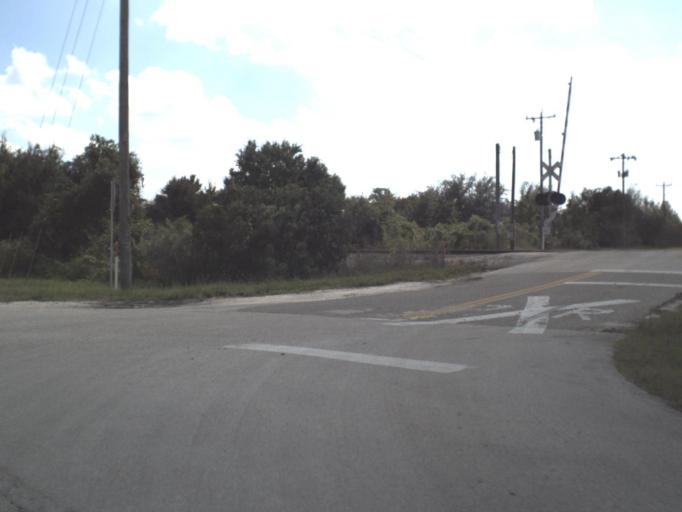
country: US
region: Florida
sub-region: Highlands County
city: Lake Placid
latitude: 27.4215
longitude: -81.2072
